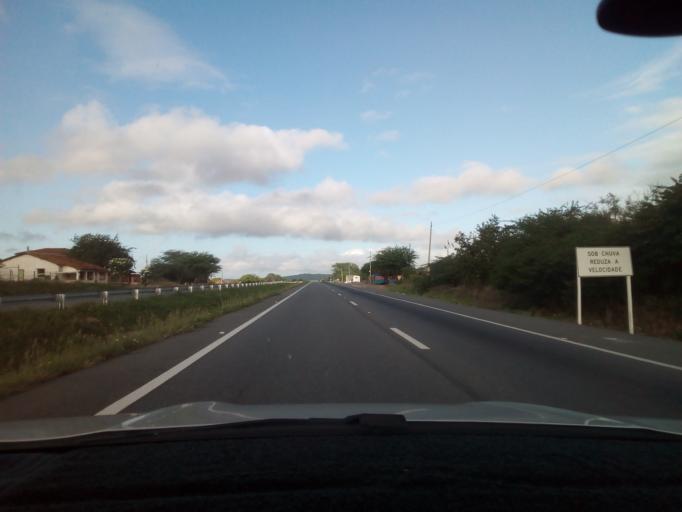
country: BR
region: Paraiba
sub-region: Serra Redonda
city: Alagoa Grande
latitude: -7.2045
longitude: -35.5623
